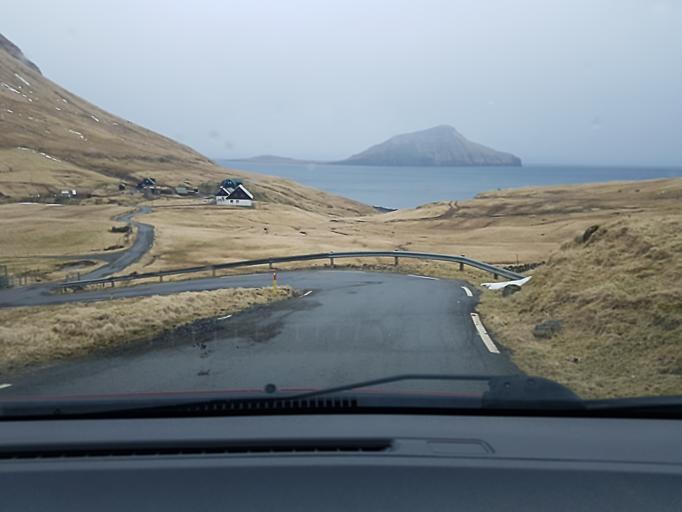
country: FO
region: Streymoy
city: Kollafjordhur
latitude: 62.0426
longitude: -6.9260
